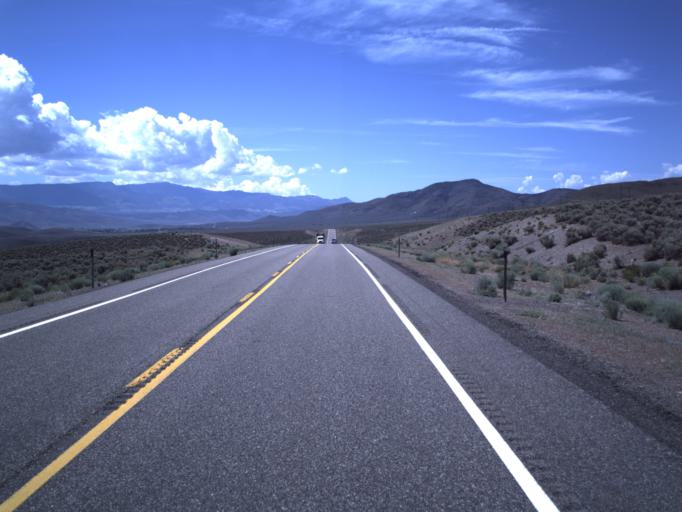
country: US
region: Utah
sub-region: Piute County
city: Junction
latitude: 38.3123
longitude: -112.2219
